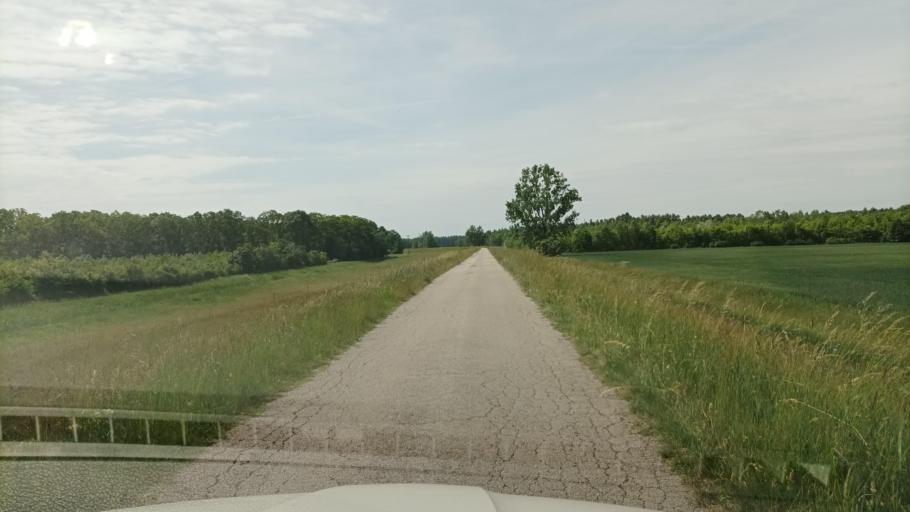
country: HU
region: Fejer
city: Racalmas
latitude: 47.0688
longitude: 18.9518
